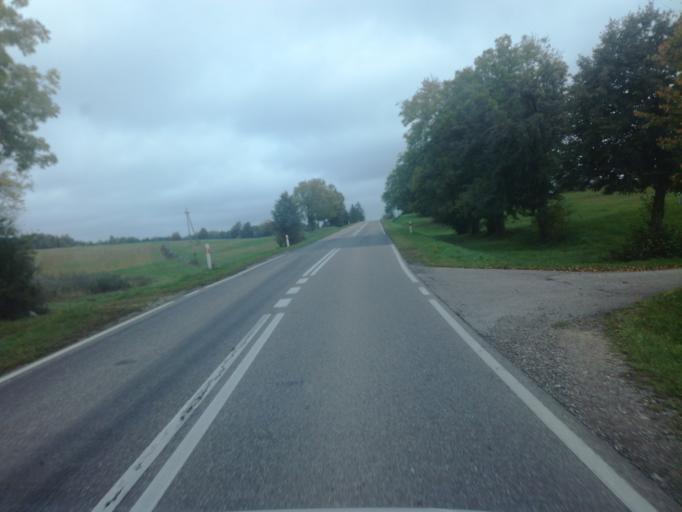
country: PL
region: Podlasie
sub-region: Powiat sejnenski
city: Sejny
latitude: 54.1221
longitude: 23.4319
